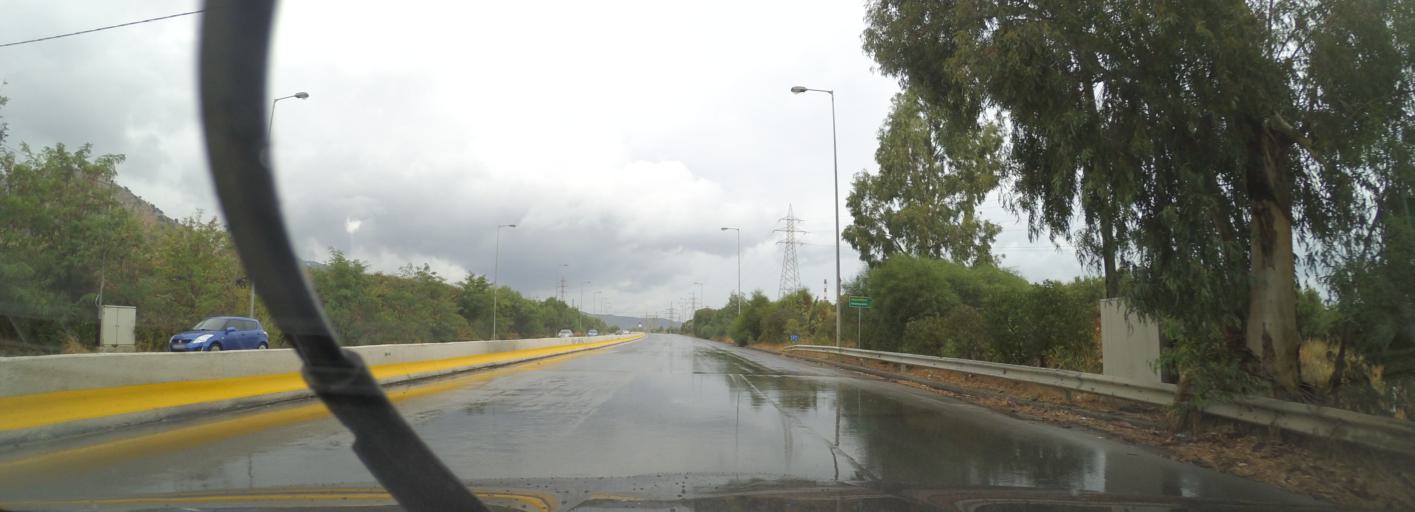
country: GR
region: Crete
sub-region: Nomos Irakleiou
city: Gazi
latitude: 35.3350
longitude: 25.0517
